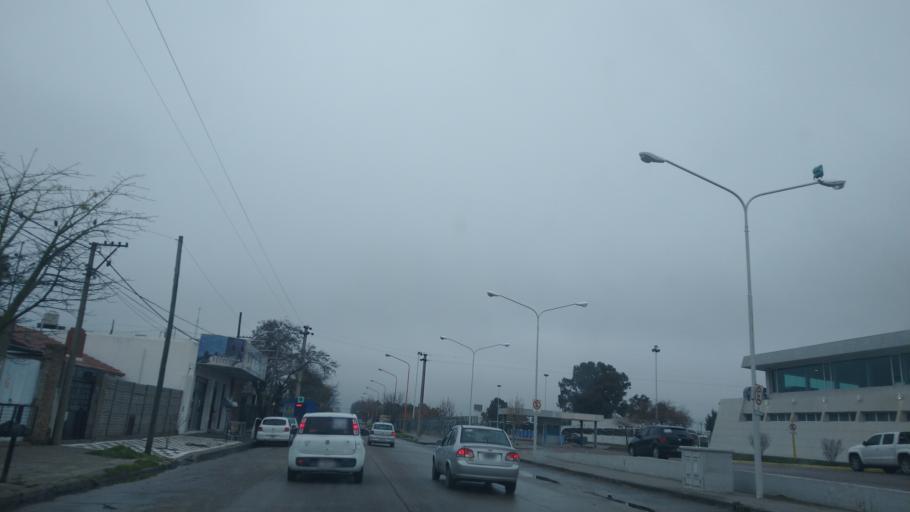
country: AR
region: Buenos Aires
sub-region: Partido de Bahia Blanca
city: Bahia Blanca
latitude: -38.7453
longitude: -62.2355
